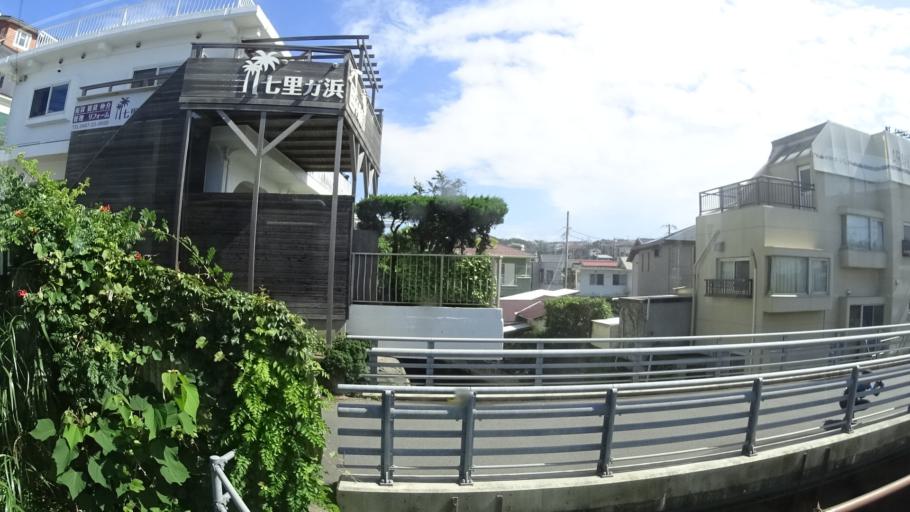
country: JP
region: Kanagawa
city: Kamakura
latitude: 35.3064
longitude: 139.5108
